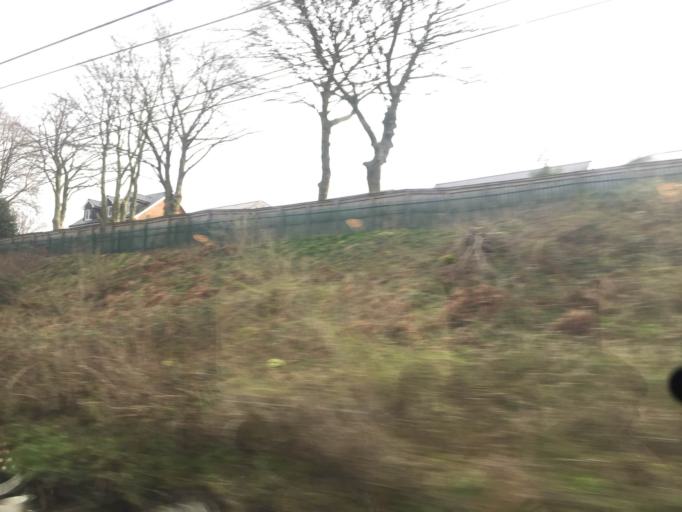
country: GB
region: England
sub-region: Borough of Wigan
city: Ince-in-Makerfield
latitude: 53.5708
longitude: -2.6399
